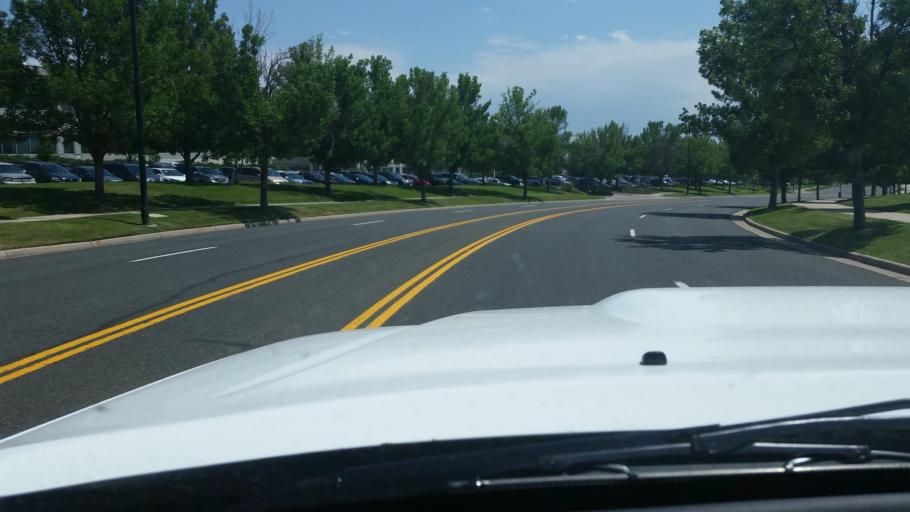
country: US
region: Colorado
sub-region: Broomfield County
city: Broomfield
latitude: 39.8966
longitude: -105.1114
